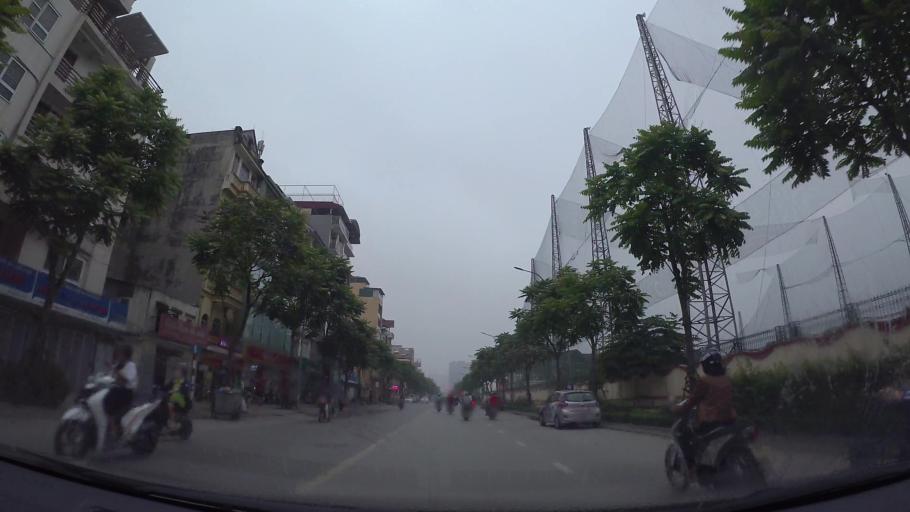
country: VN
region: Ha Noi
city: Hai BaTrung
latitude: 20.9902
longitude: 105.8338
